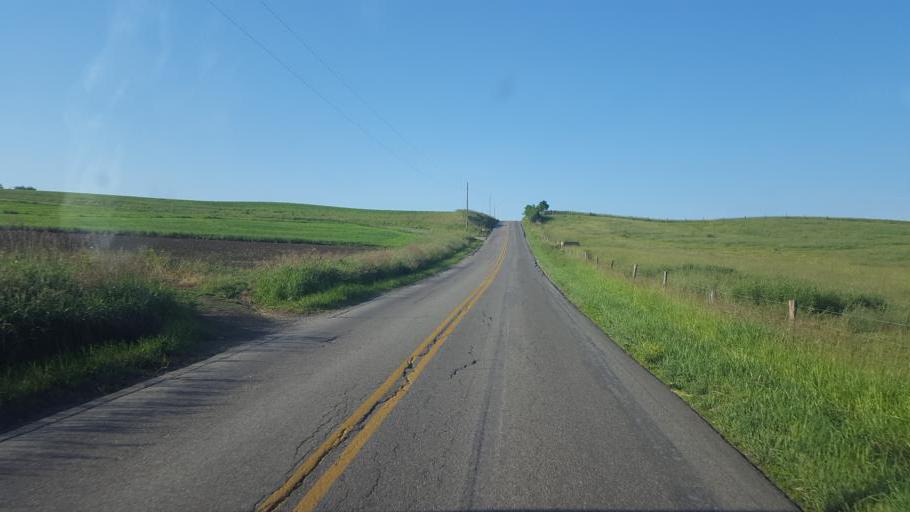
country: US
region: Ohio
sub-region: Wayne County
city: Apple Creek
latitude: 40.6583
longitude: -81.7843
